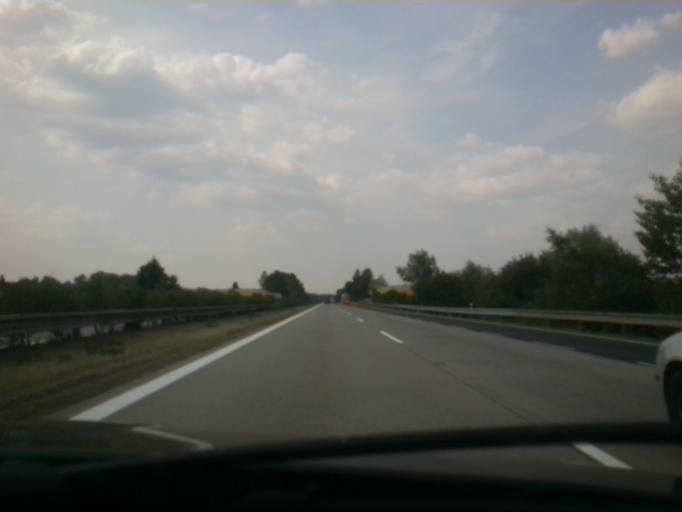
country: CZ
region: Central Bohemia
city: Divisov
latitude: 49.8204
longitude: 14.8731
